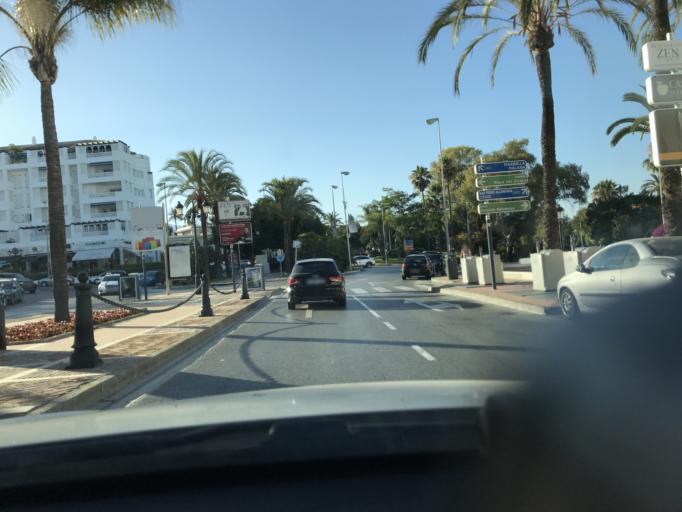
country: ES
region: Andalusia
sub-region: Provincia de Malaga
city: Marbella
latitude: 36.4878
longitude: -4.9562
